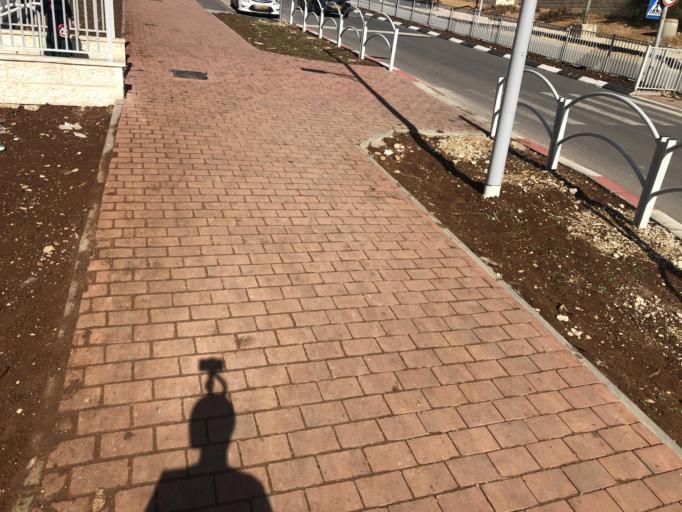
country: IL
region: Jerusalem
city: Modiin Ilit
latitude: 31.9274
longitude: 35.0458
